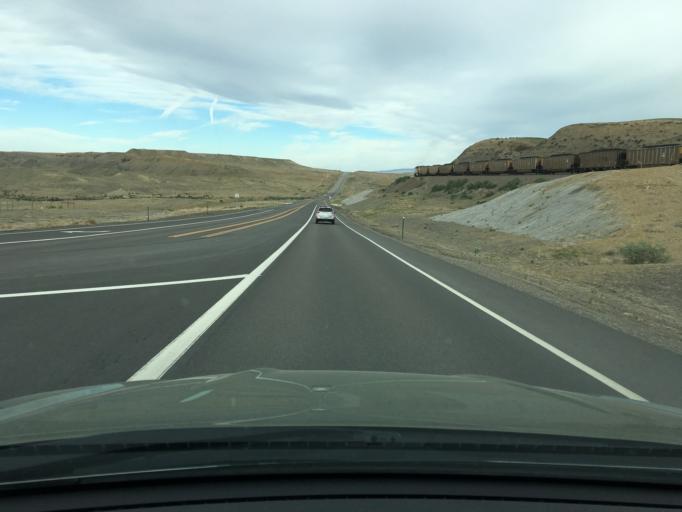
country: US
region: Colorado
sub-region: Delta County
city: Cedaredge
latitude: 38.7971
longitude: -107.8326
